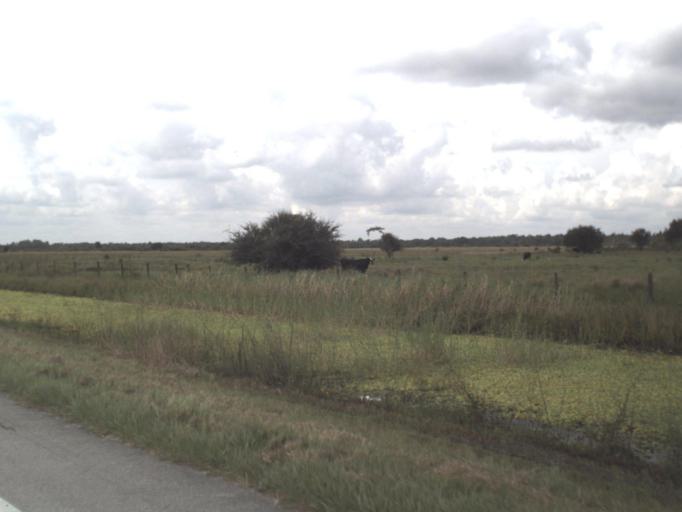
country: US
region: Florida
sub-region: Hendry County
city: Port LaBelle
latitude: 26.8563
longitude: -81.3750
